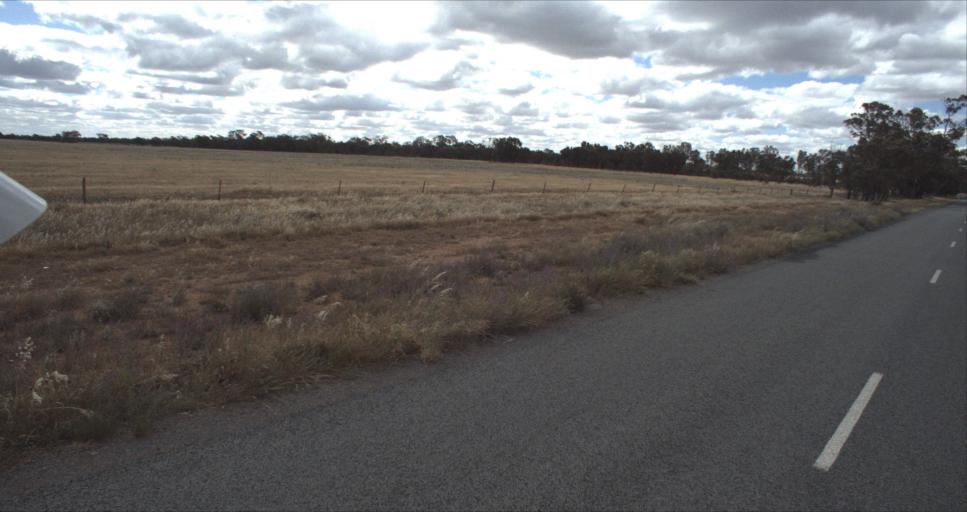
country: AU
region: New South Wales
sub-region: Leeton
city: Leeton
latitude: -34.6693
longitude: 146.3478
